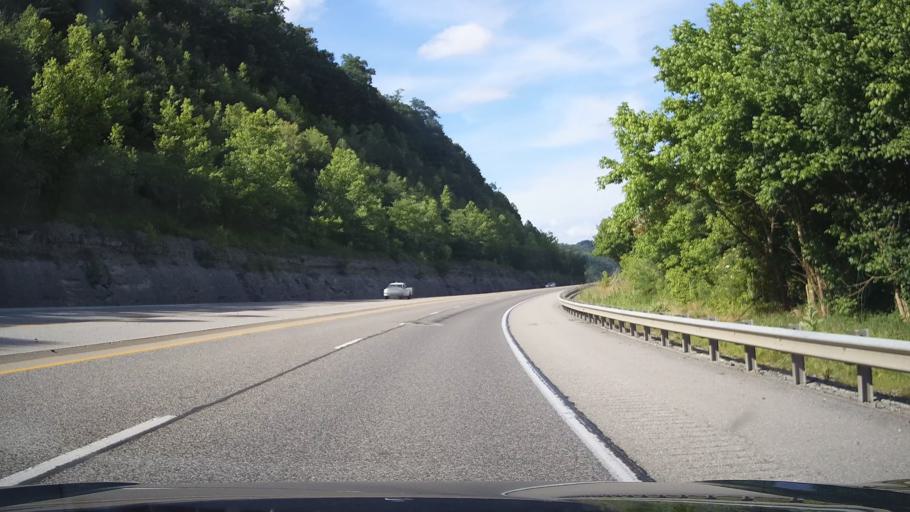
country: US
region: Kentucky
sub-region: Lawrence County
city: Louisa
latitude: 38.0100
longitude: -82.6646
